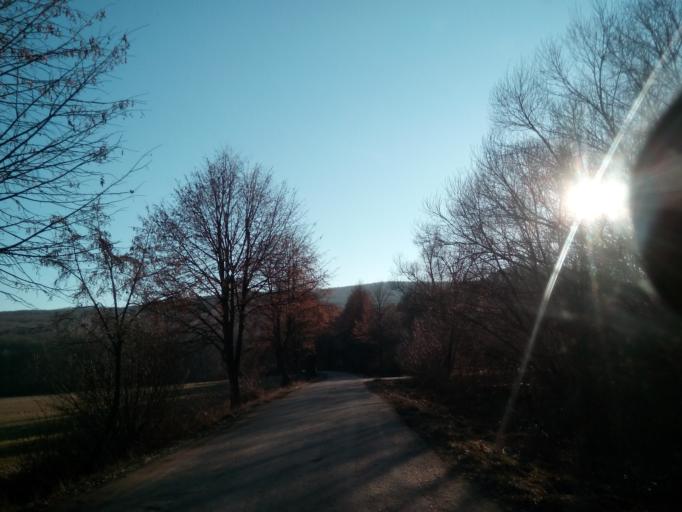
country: SK
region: Kosicky
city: Medzev
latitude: 48.6953
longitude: 20.9194
